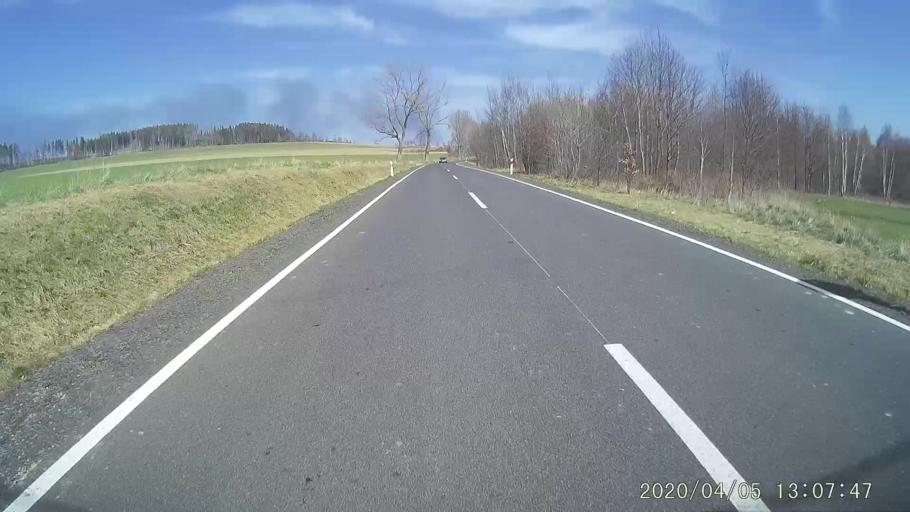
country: PL
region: Lower Silesian Voivodeship
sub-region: Powiat lubanski
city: Lesna
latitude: 50.9806
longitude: 15.3112
